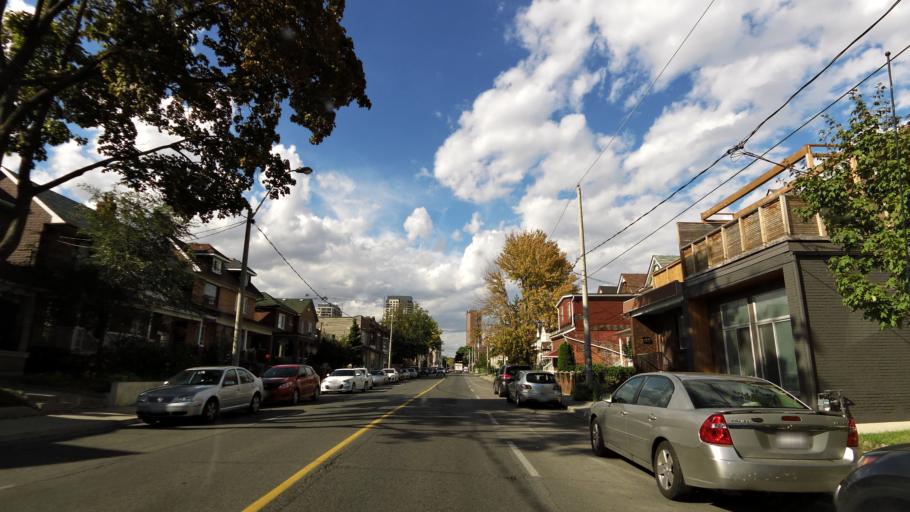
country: CA
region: Ontario
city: Toronto
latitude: 43.6627
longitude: -79.4449
